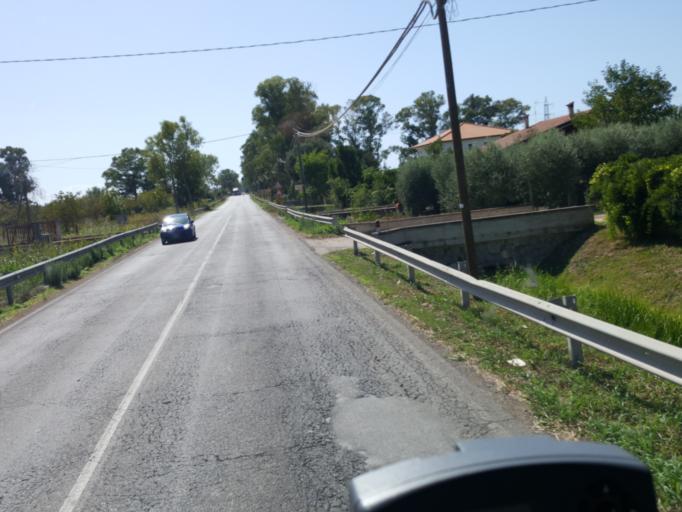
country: IT
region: Latium
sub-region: Provincia di Latina
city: Borgo Hermada
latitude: 41.3672
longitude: 13.1196
